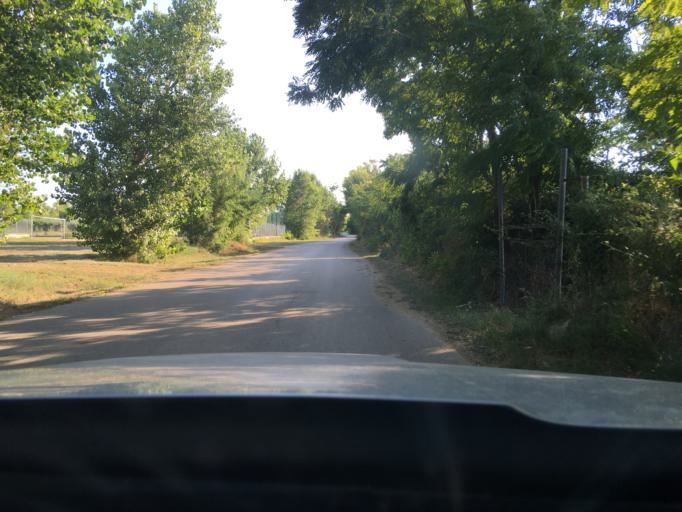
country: HR
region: Zadarska
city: Nin
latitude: 44.2521
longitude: 15.1539
